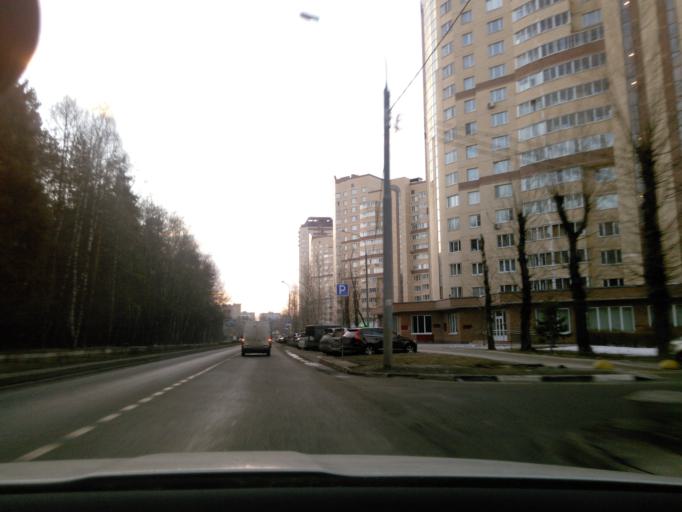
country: RU
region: Moskovskaya
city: Mendeleyevo
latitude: 56.0007
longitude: 37.2143
